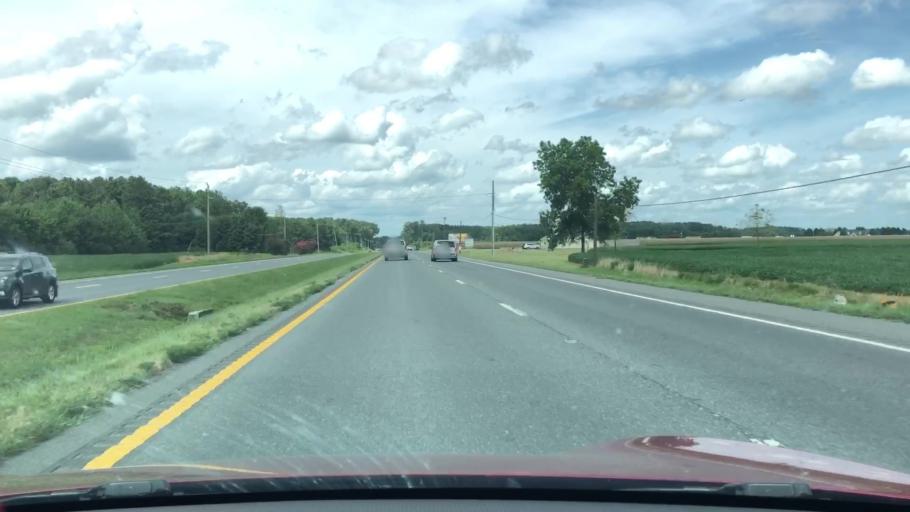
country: US
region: Virginia
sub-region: Accomack County
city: Wattsville
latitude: 37.9107
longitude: -75.5490
